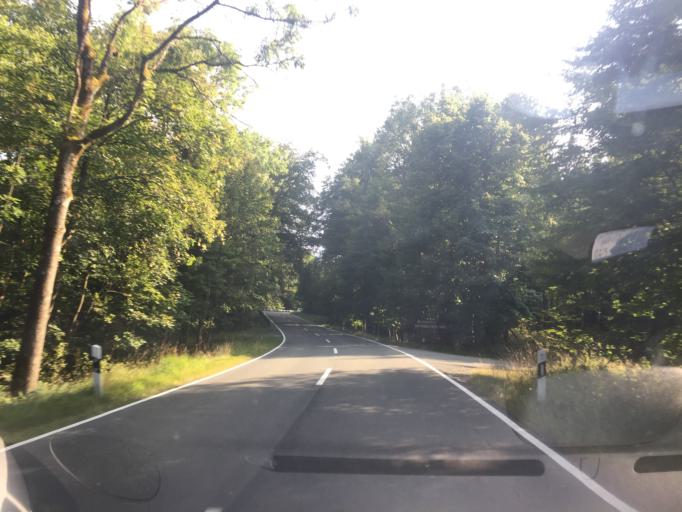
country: DE
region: Saxony-Anhalt
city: Darlingerode
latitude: 51.7785
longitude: 10.7322
